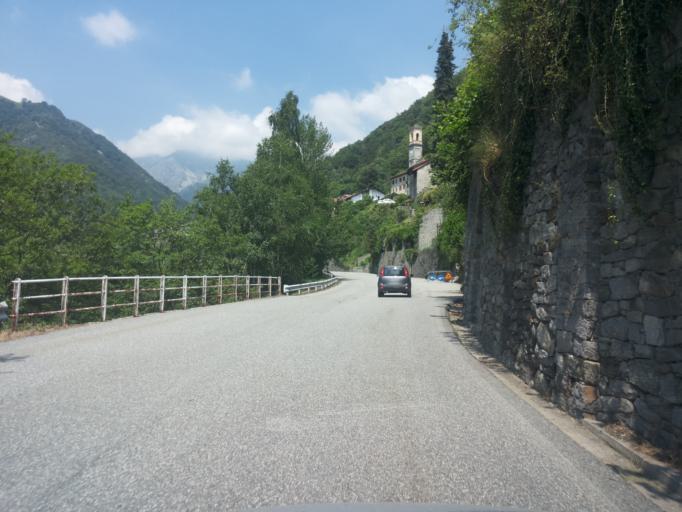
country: IT
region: Piedmont
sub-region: Provincia di Biella
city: Rosazza
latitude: 45.6712
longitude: 7.9886
